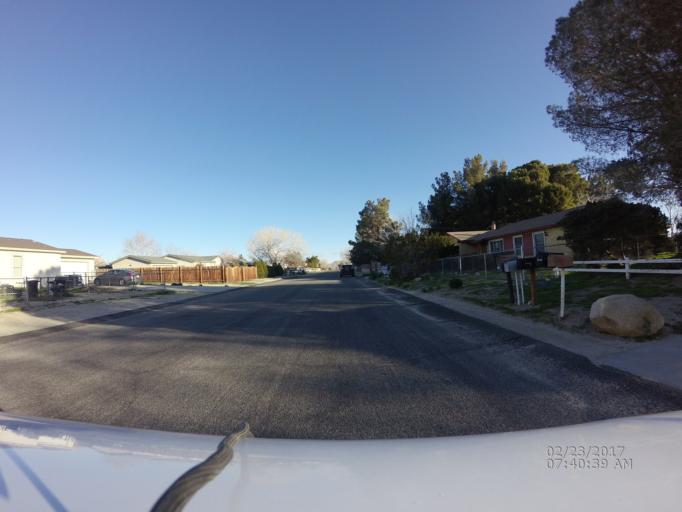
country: US
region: California
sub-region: Los Angeles County
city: Lake Los Angeles
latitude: 34.6107
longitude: -117.8104
